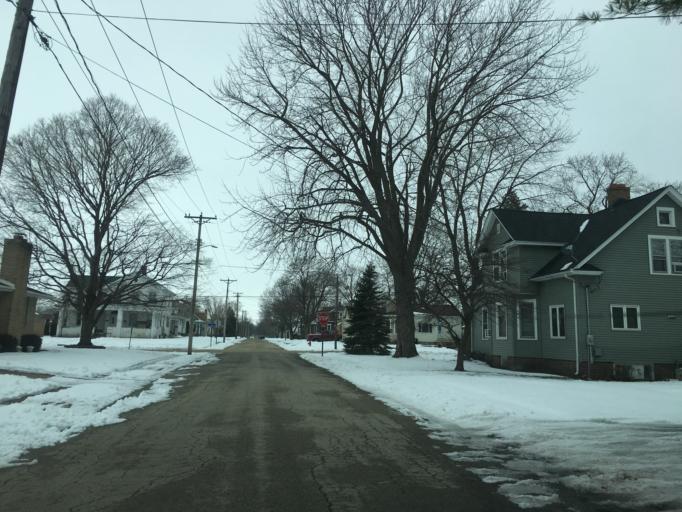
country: US
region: Illinois
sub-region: LaSalle County
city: Peru
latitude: 41.3298
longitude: -89.1318
